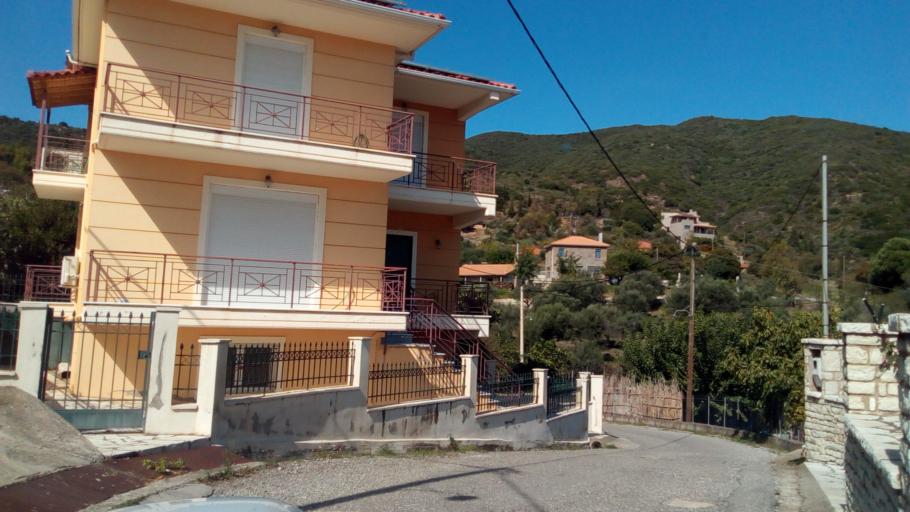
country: GR
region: West Greece
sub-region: Nomos Aitolias kai Akarnanias
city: Antirrio
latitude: 38.3591
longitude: 21.7532
